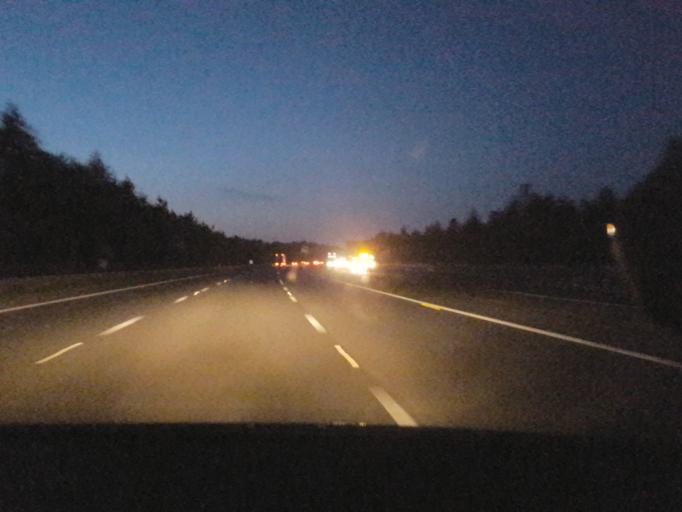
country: GB
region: England
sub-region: Leicestershire
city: Shepshed
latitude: 52.7322
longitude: -1.2823
